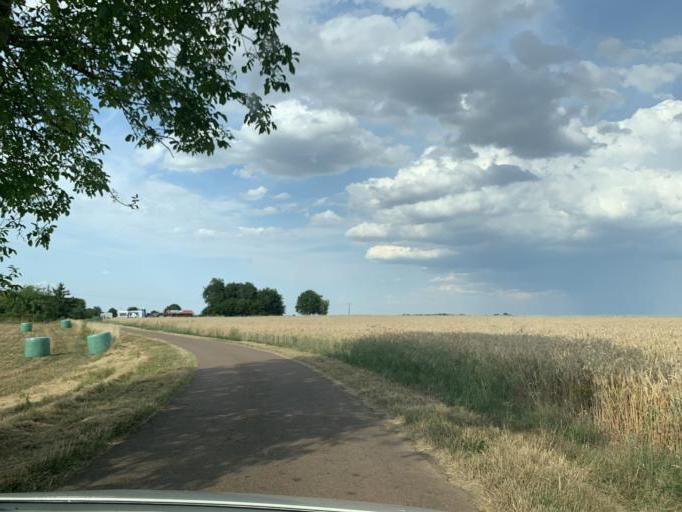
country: FR
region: Bourgogne
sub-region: Departement de l'Yonne
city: Fontenailles
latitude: 47.5149
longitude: 3.4272
